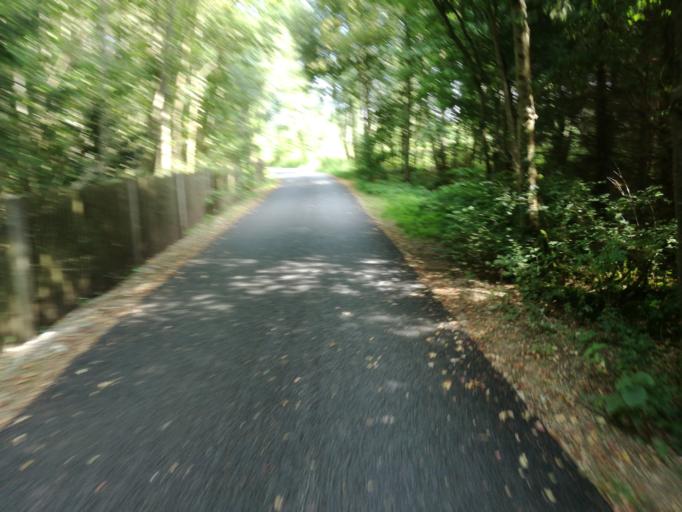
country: DE
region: Bavaria
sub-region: Upper Bavaria
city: Grafelfing
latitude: 48.1264
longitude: 11.4164
